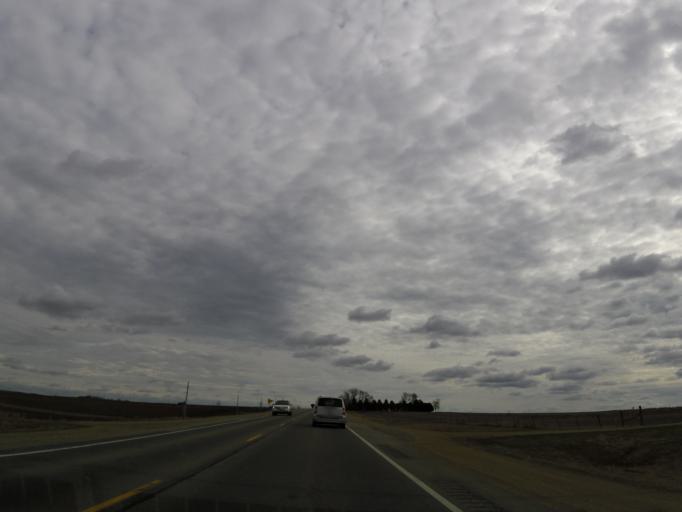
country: US
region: Iowa
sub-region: Chickasaw County
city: New Hampton
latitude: 43.1627
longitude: -92.2989
